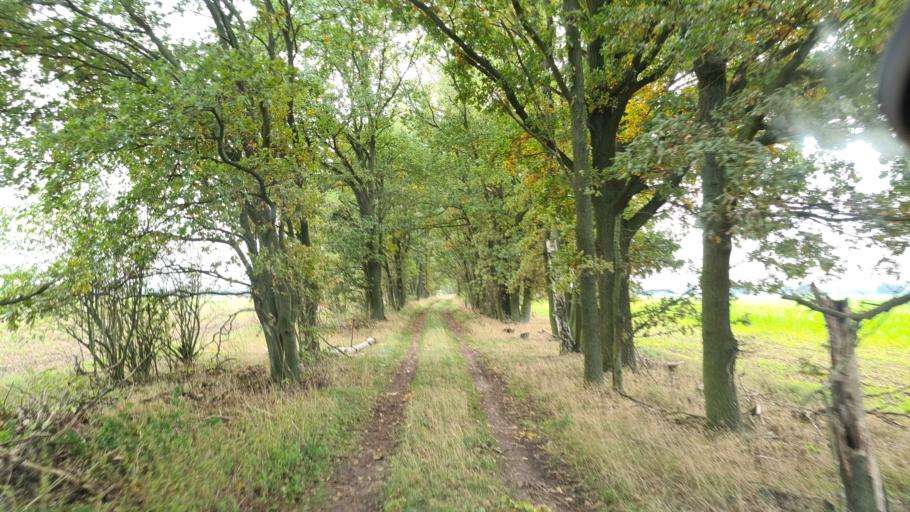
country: DE
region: Brandenburg
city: Schonewalde
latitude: 51.6833
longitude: 13.5620
